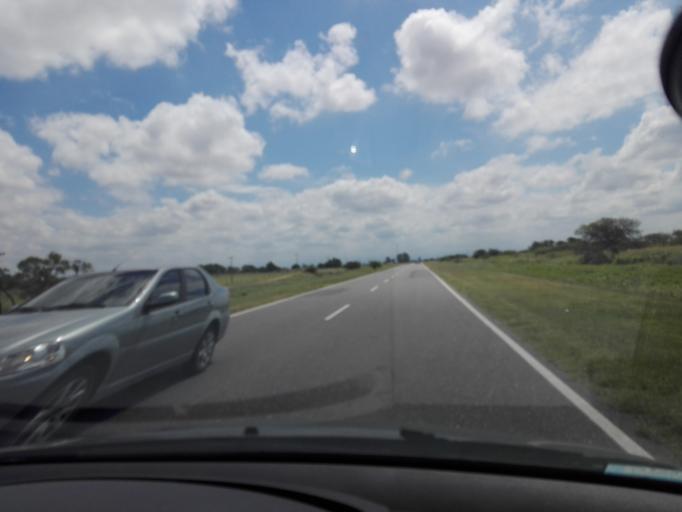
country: AR
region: Cordoba
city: Toledo
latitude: -31.6470
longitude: -64.0674
